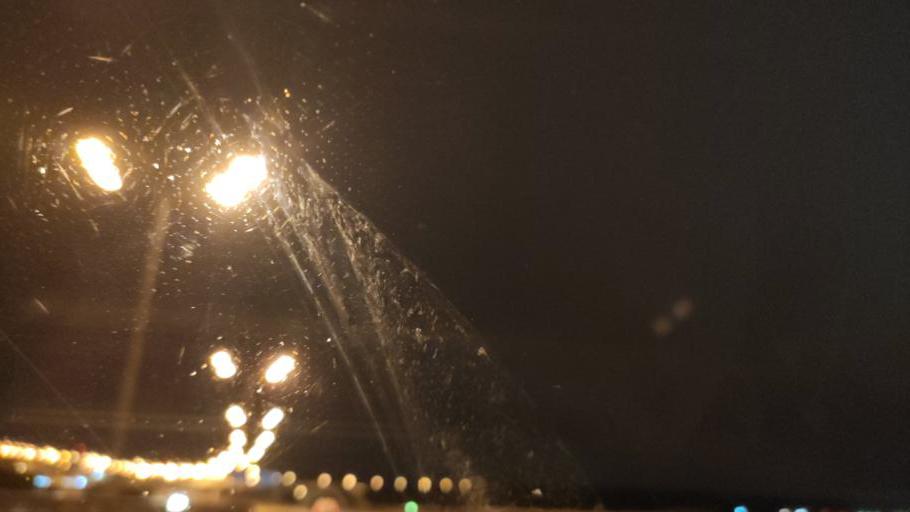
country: RU
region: Moscow
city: Vnukovo
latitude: 55.5822
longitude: 37.2084
